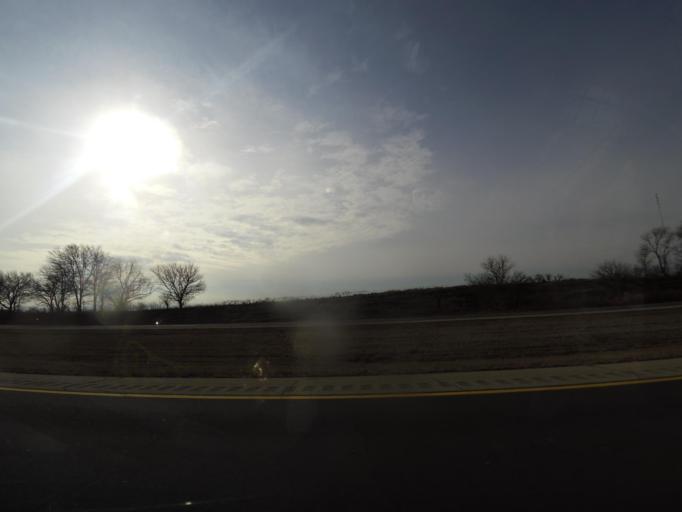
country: US
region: Illinois
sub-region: Macon County
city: Decatur
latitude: 39.7881
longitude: -88.9864
